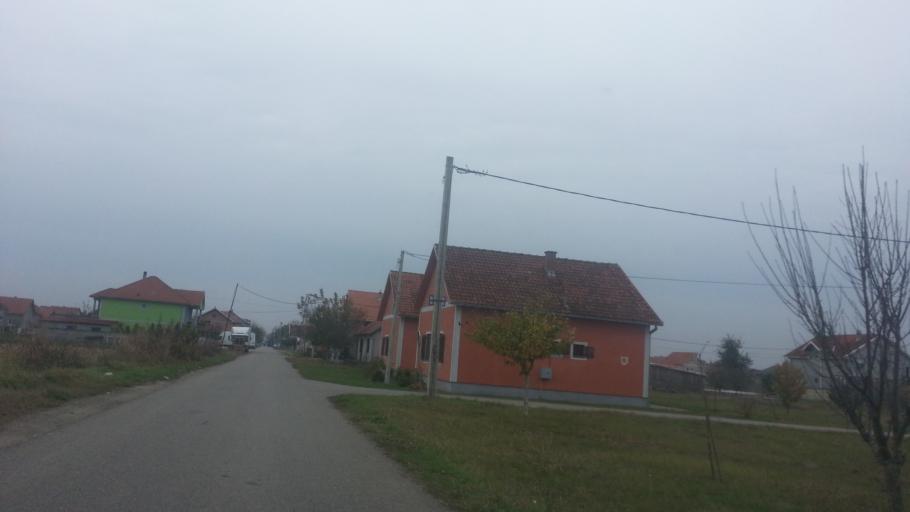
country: RS
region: Autonomna Pokrajina Vojvodina
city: Nova Pazova
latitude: 44.9576
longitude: 20.2147
